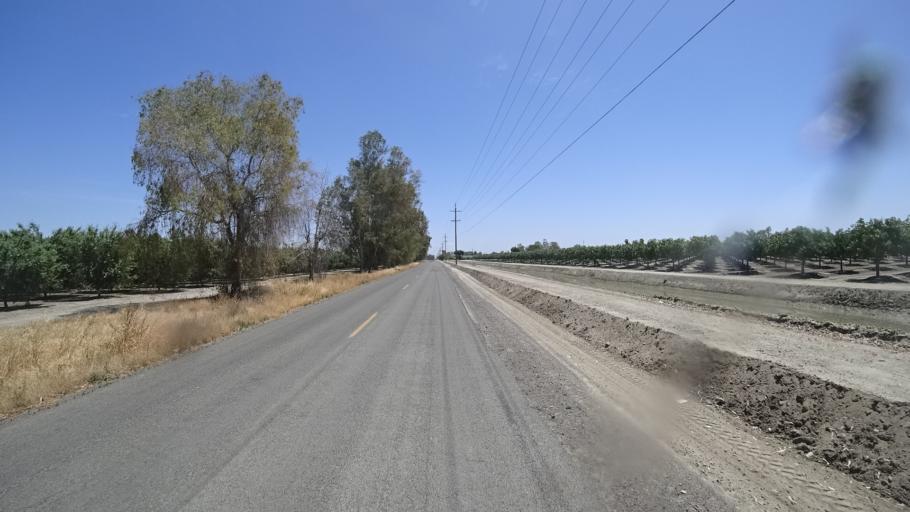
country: US
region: California
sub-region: Kings County
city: Corcoran
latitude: 36.1090
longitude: -119.5931
